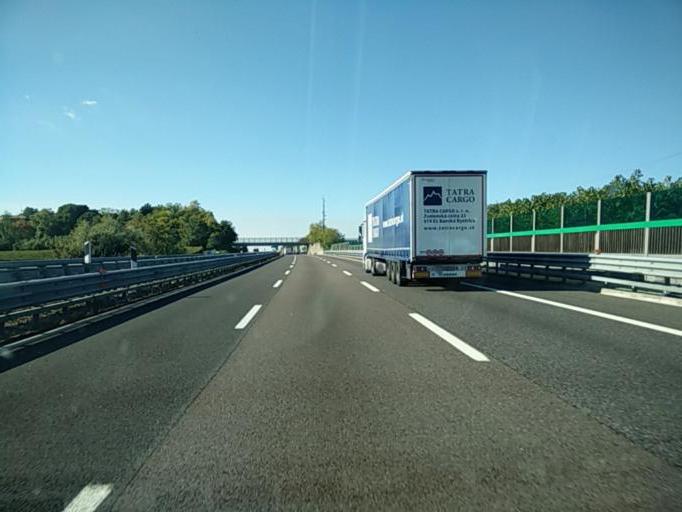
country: IT
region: Veneto
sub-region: Provincia di Verona
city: Cavalcaselle
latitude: 45.4293
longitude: 10.7307
